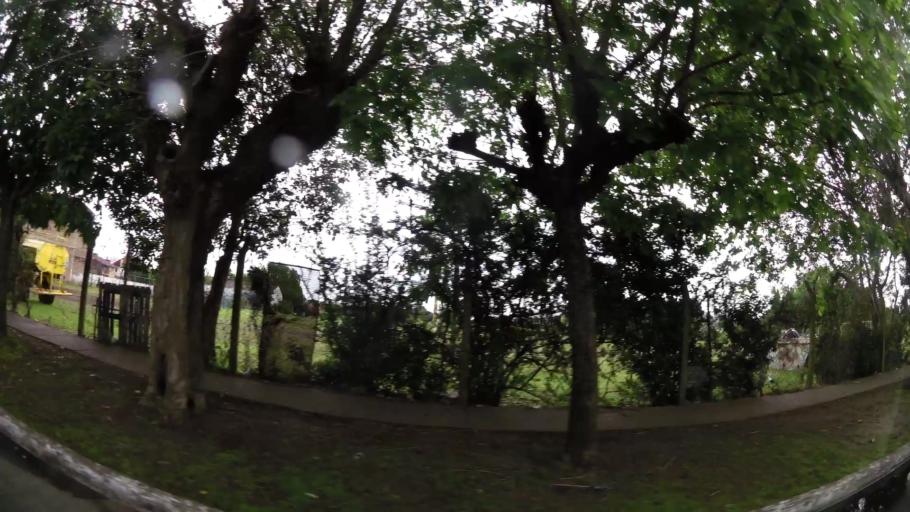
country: AR
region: Buenos Aires
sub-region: Partido de Quilmes
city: Quilmes
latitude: -34.7720
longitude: -58.2186
